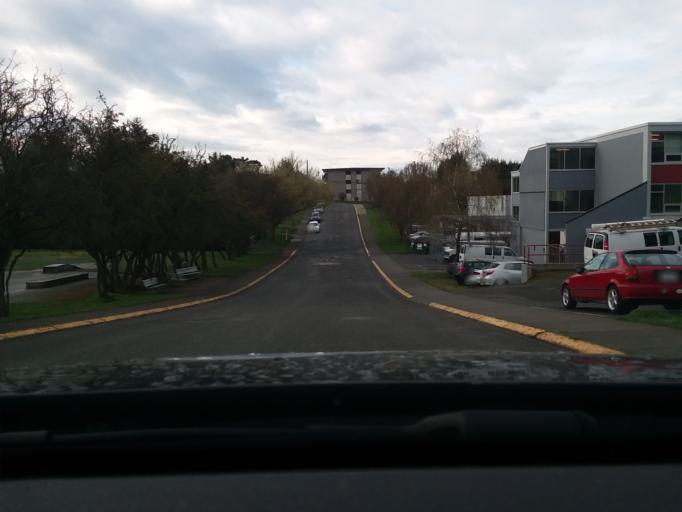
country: CA
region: British Columbia
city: Victoria
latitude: 48.4388
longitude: -123.3959
